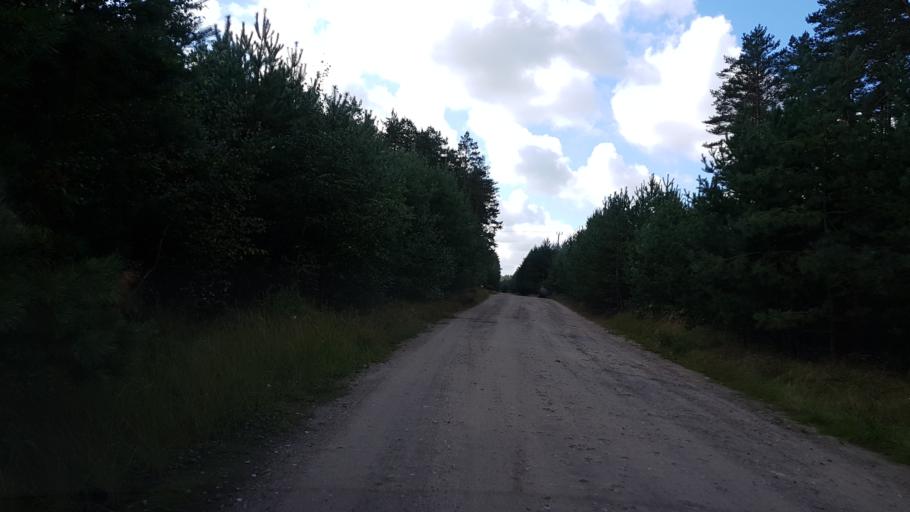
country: PL
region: West Pomeranian Voivodeship
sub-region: Powiat bialogardzki
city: Tychowo
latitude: 54.0417
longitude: 16.3084
